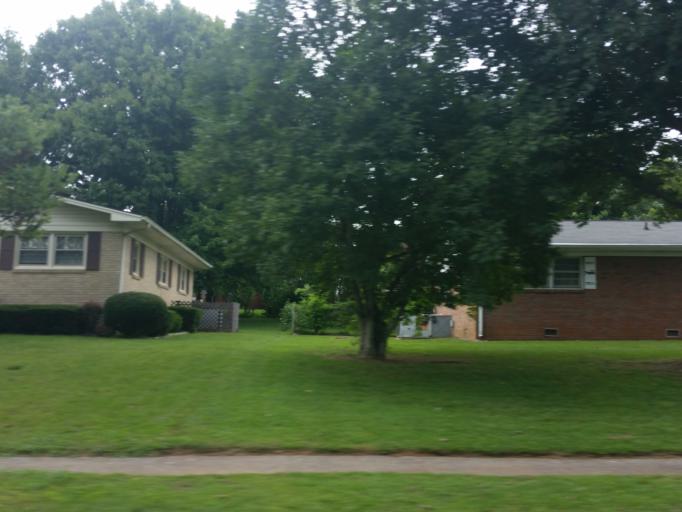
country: US
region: Kentucky
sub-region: Christian County
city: Hopkinsville
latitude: 36.8514
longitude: -87.5176
